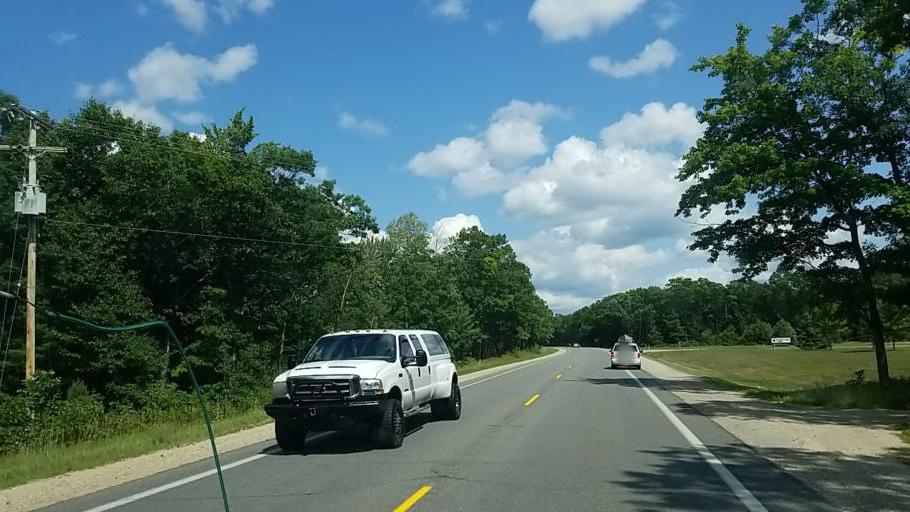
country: US
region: Michigan
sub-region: Newaygo County
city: Newaygo
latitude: 43.4049
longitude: -85.7650
